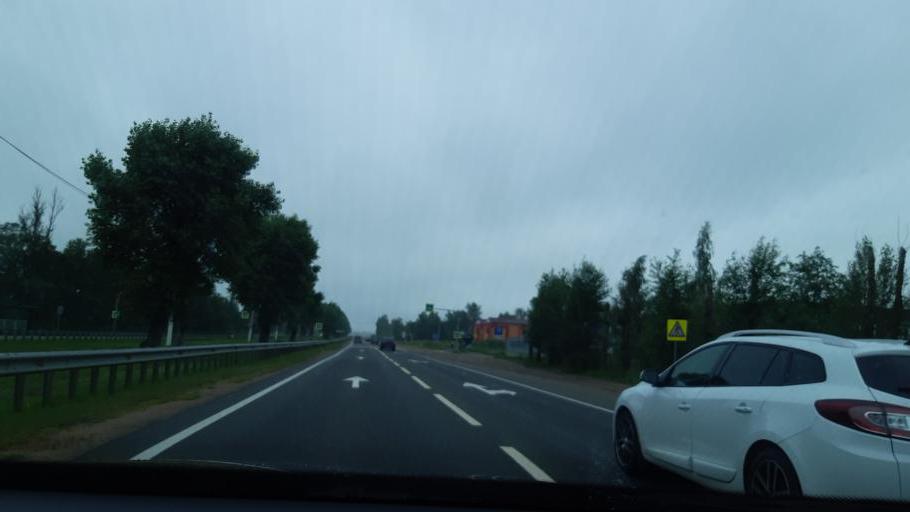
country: RU
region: Smolensk
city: Talashkino
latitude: 54.6845
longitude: 32.1373
